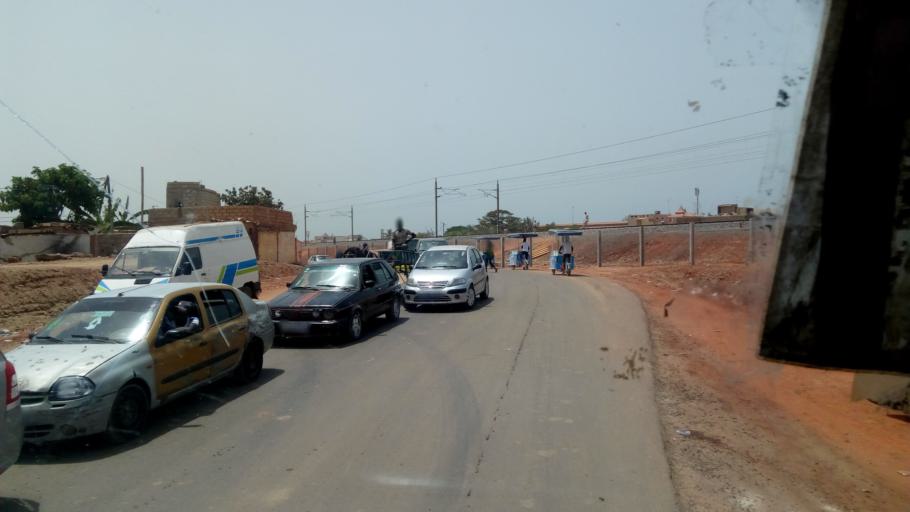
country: SN
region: Dakar
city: Pikine
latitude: 14.7215
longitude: -17.2814
